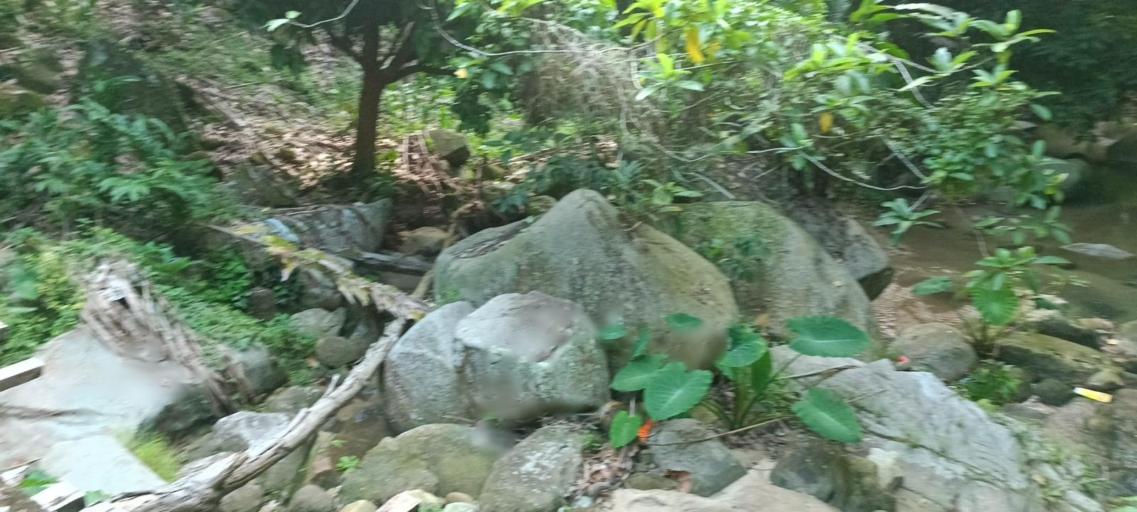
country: MY
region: Penang
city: Kampung Sungai Ara
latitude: 5.3227
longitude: 100.2560
